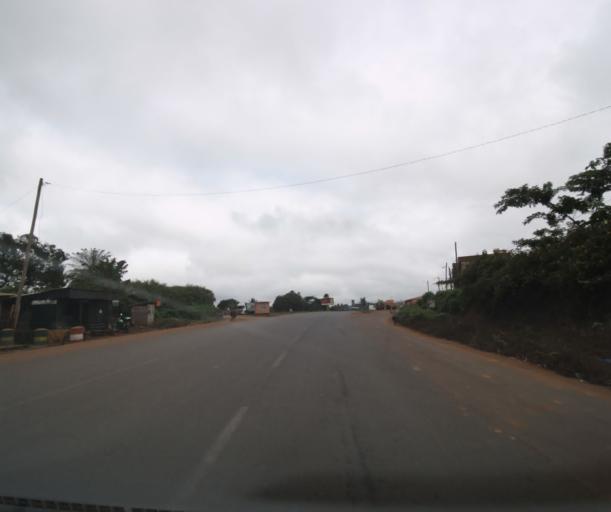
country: CM
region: Centre
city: Mbankomo
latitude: 3.7872
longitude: 11.4258
